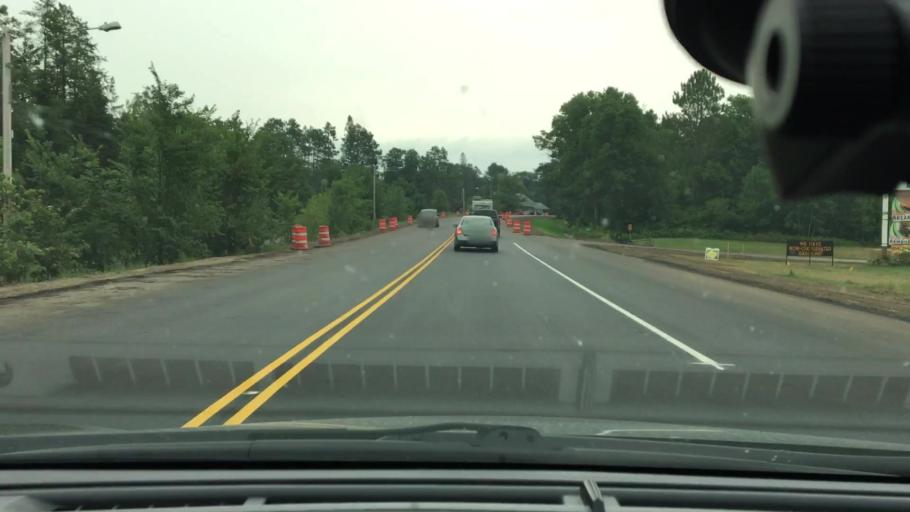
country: US
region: Minnesota
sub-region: Crow Wing County
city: Cross Lake
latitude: 46.7361
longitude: -93.9605
